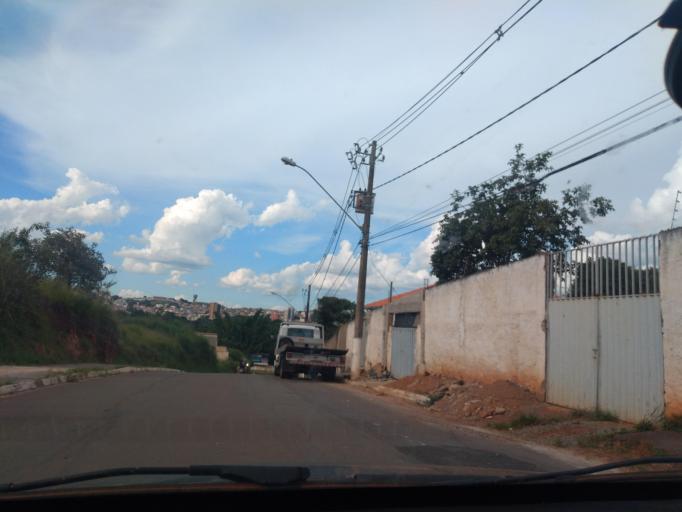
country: BR
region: Minas Gerais
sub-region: Tres Coracoes
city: Tres Coracoes
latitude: -21.7086
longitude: -45.2611
